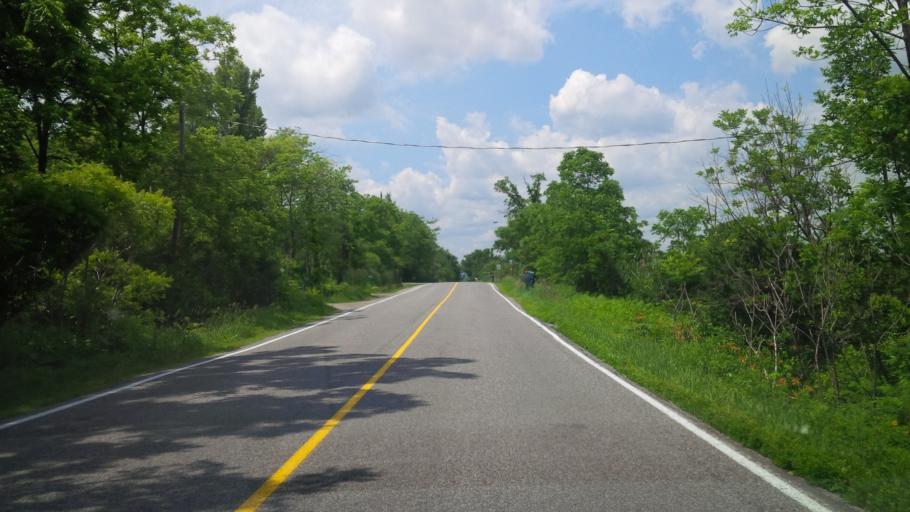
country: CA
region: Ontario
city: Burlington
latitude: 43.4238
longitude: -79.8683
